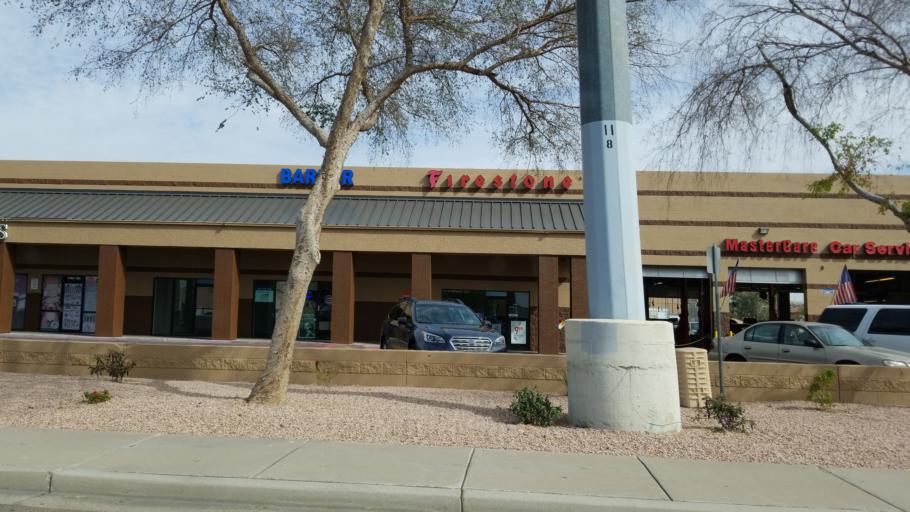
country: US
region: Arizona
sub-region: Maricopa County
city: Glendale
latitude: 33.6538
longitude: -112.0654
